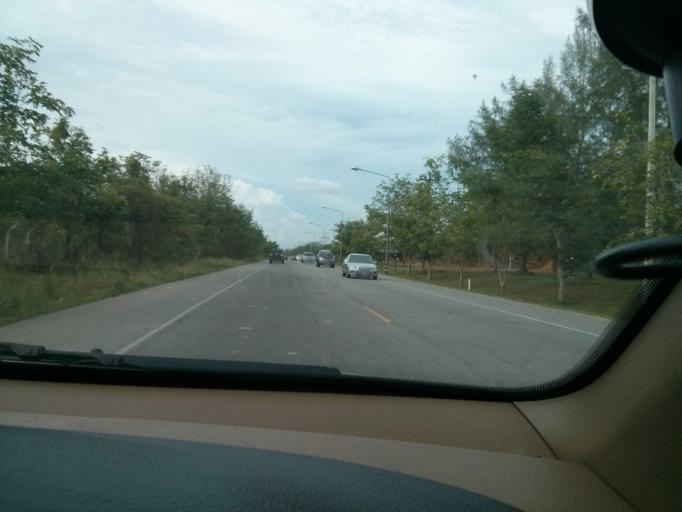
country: TH
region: Chon Buri
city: Sattahip
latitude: 12.6638
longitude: 100.9700
